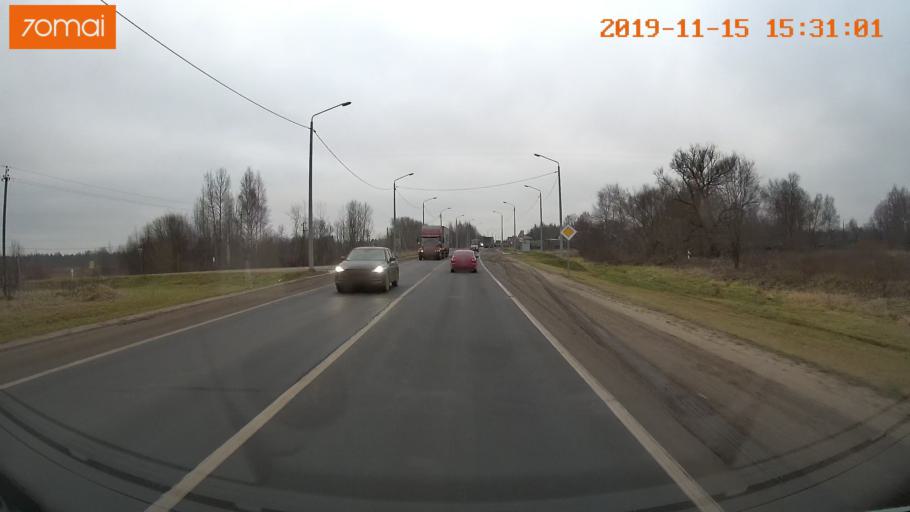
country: RU
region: Jaroslavl
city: Danilov
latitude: 58.1042
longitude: 40.1102
